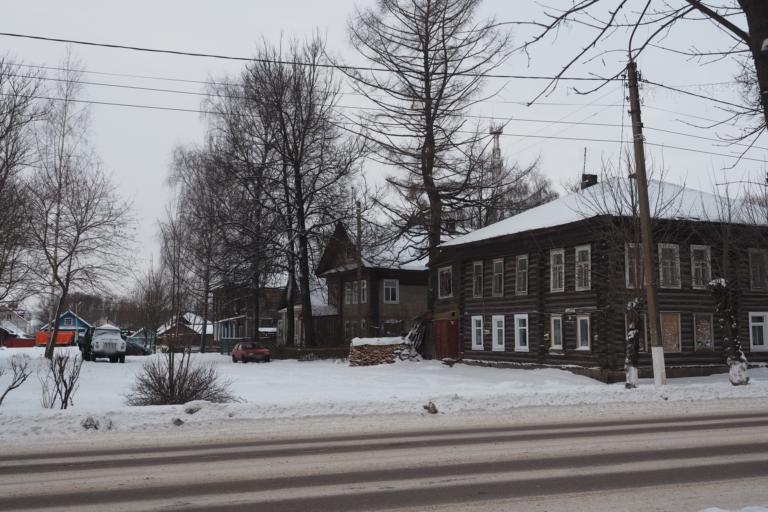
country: RU
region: Tverskaya
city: Bezhetsk
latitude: 57.7895
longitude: 36.6905
